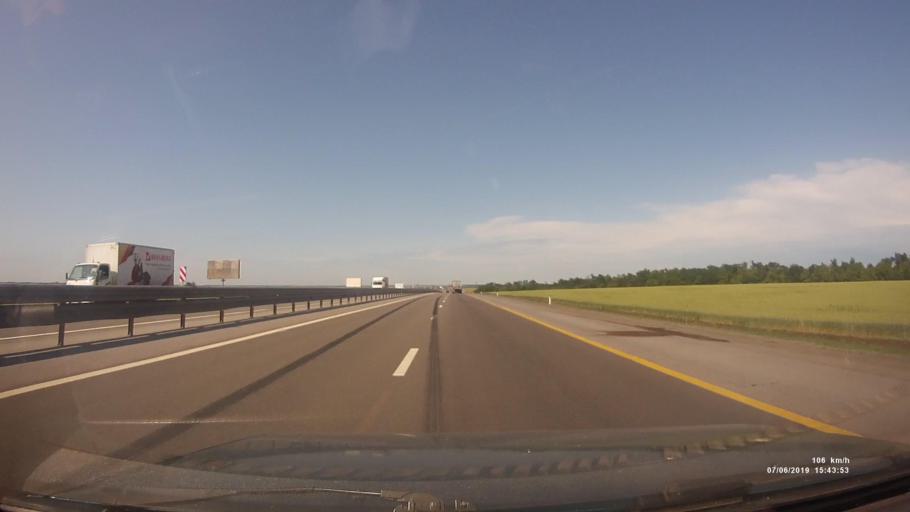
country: RU
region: Rostov
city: Mayskiy
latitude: 47.7216
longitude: 40.1112
